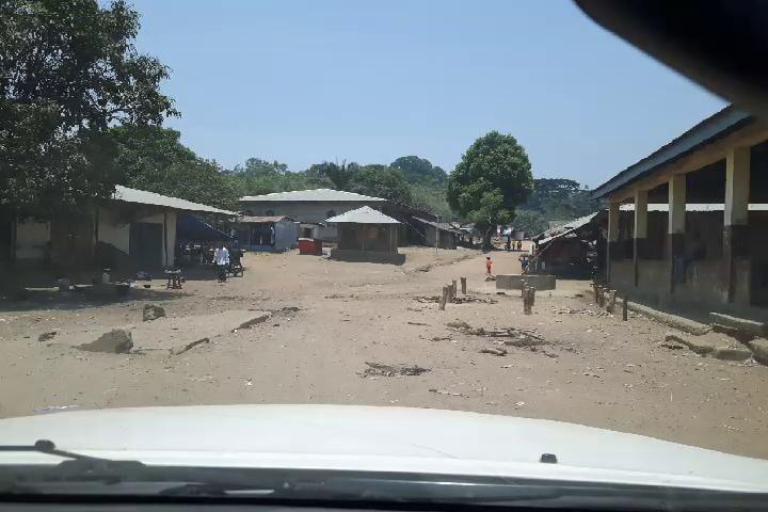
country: SL
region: Northern Province
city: Alikalia
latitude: 9.1534
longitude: -11.3875
